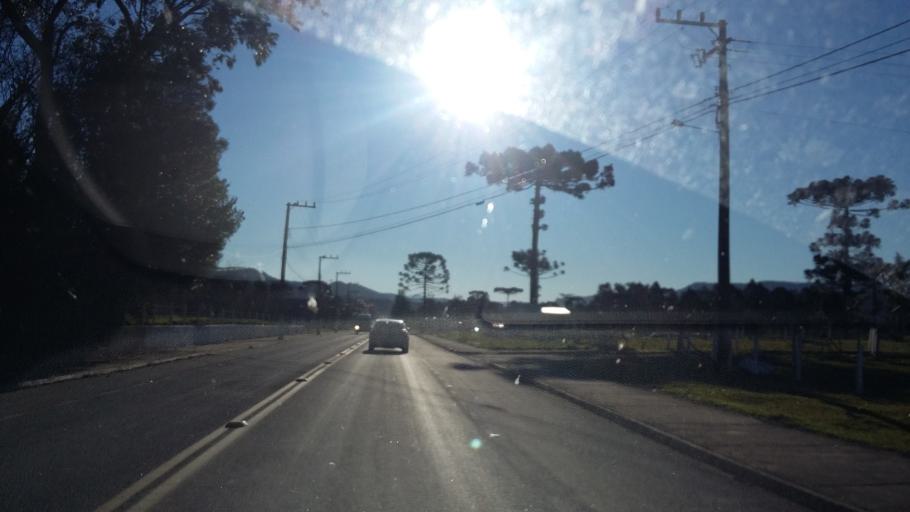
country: BR
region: Santa Catarina
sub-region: Lauro Muller
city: Lauro Muller
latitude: -27.9935
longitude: -49.5719
